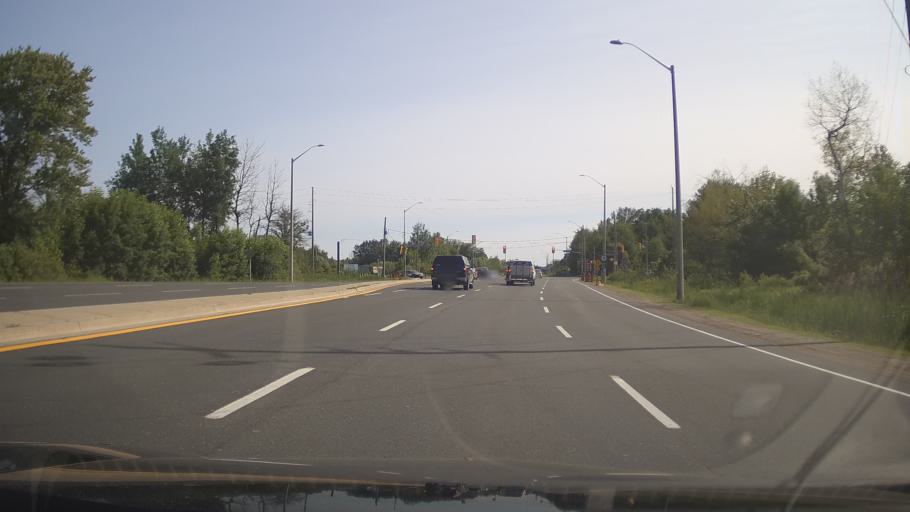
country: CA
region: Ontario
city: Peterborough
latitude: 44.2685
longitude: -78.3461
